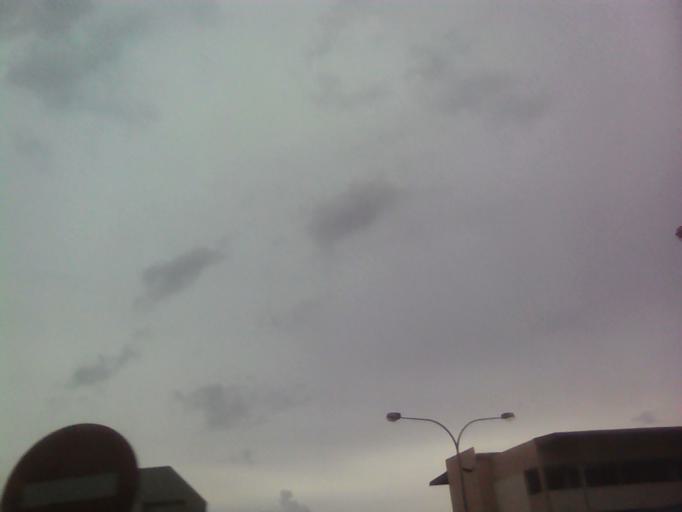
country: MY
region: Penang
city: Butterworth
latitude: 5.4058
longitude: 100.3832
